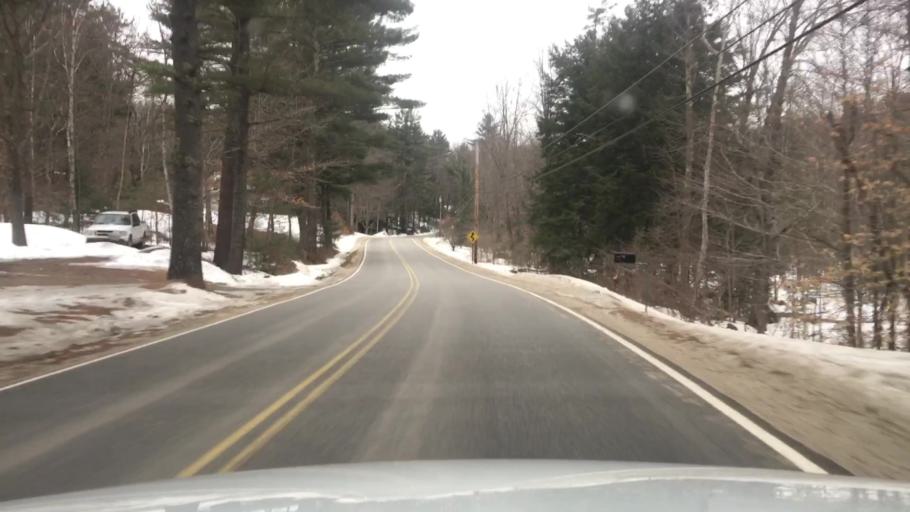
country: US
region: Maine
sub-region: York County
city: Shapleigh
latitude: 43.5090
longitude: -70.8157
